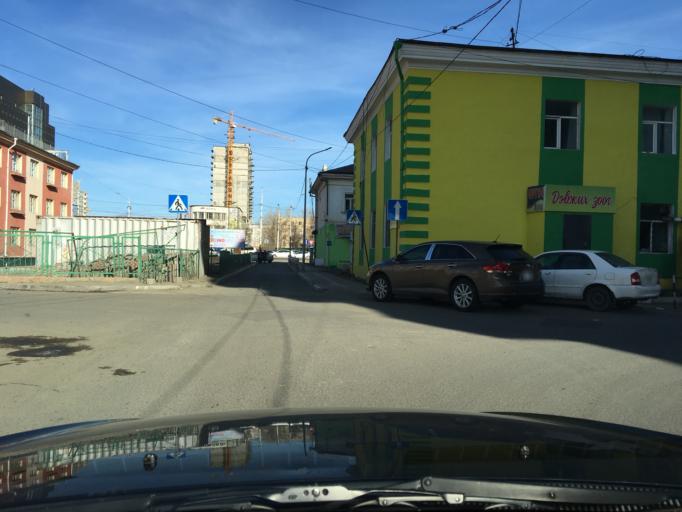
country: MN
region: Ulaanbaatar
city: Ulaanbaatar
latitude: 47.8980
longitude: 106.8939
